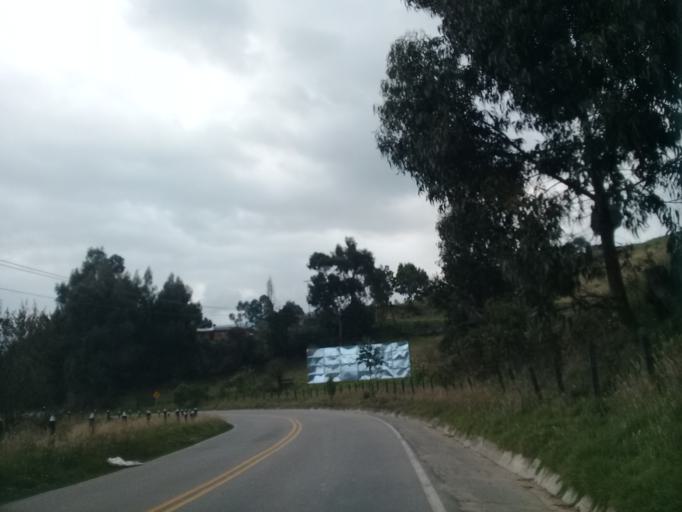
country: CO
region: Cundinamarca
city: Zipaquira
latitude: 5.0330
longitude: -74.0386
